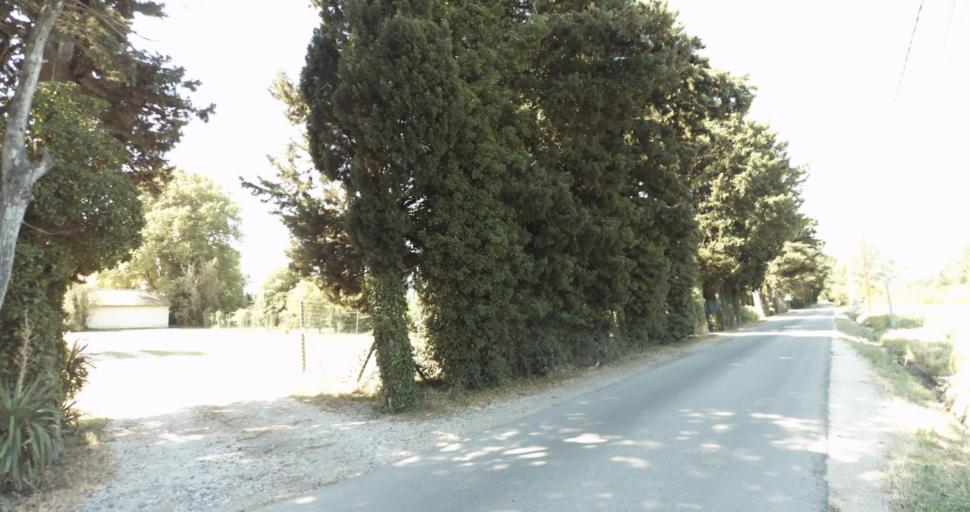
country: FR
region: Provence-Alpes-Cote d'Azur
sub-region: Departement du Vaucluse
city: Monteux
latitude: 44.0119
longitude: 5.0030
